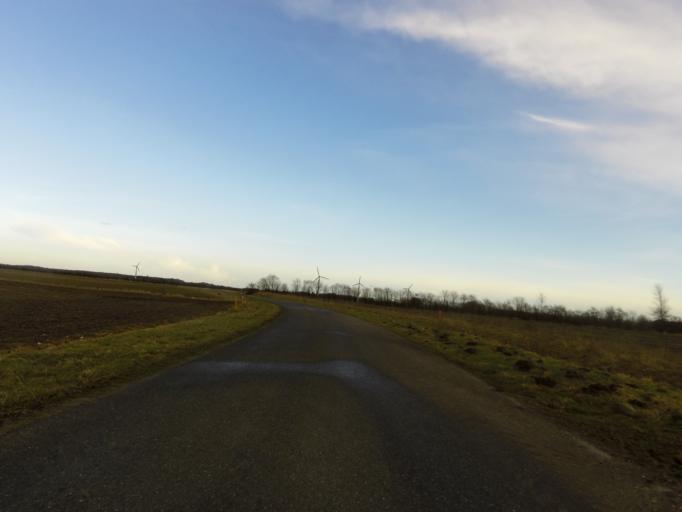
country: DK
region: South Denmark
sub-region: Tonder Kommune
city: Toftlund
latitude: 55.2394
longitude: 9.0614
